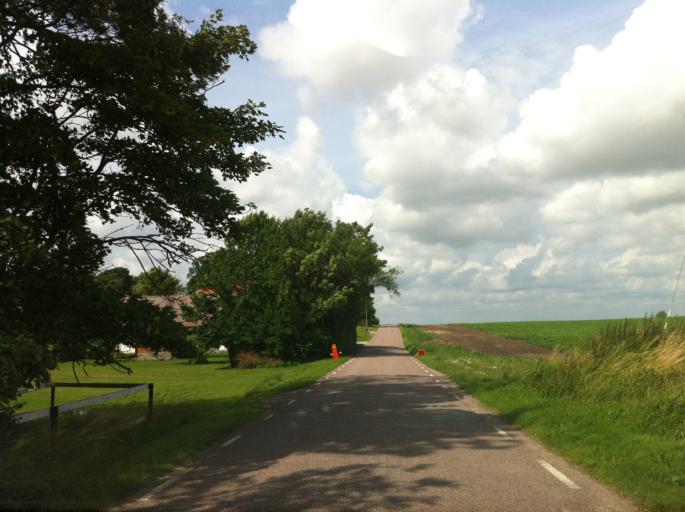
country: SE
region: Skane
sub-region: Skurups Kommun
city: Skurup
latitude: 55.4196
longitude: 13.4619
